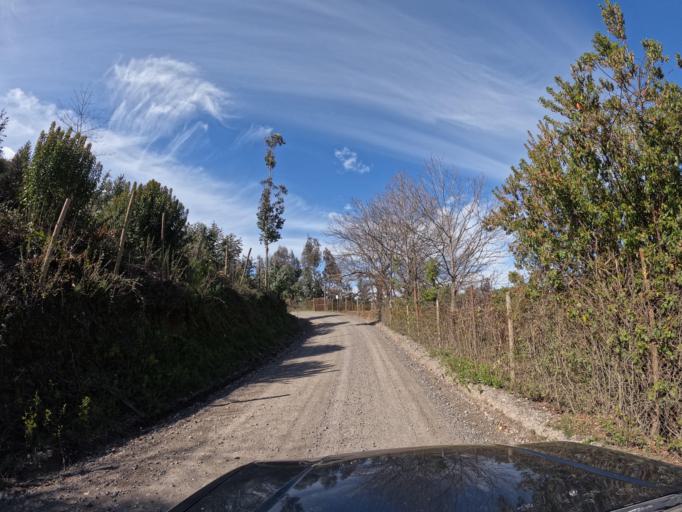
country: CL
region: Biobio
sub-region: Provincia de Concepcion
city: Chiguayante
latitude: -37.0657
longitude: -72.8978
